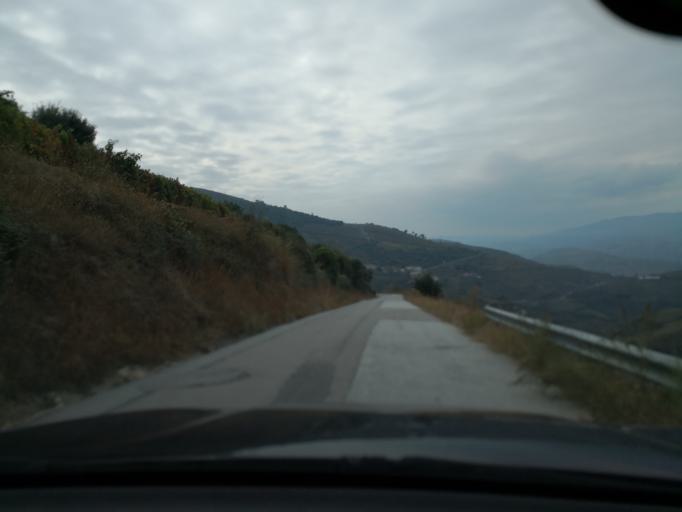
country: PT
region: Vila Real
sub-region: Peso da Regua
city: Peso da Regua
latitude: 41.1805
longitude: -7.7421
